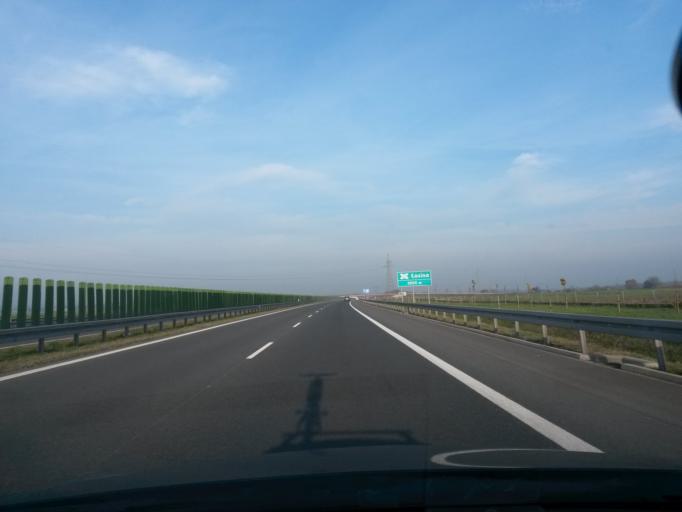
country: PL
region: Lower Silesian Voivodeship
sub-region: Powiat wroclawski
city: Mirkow
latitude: 51.2103
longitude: 17.1291
